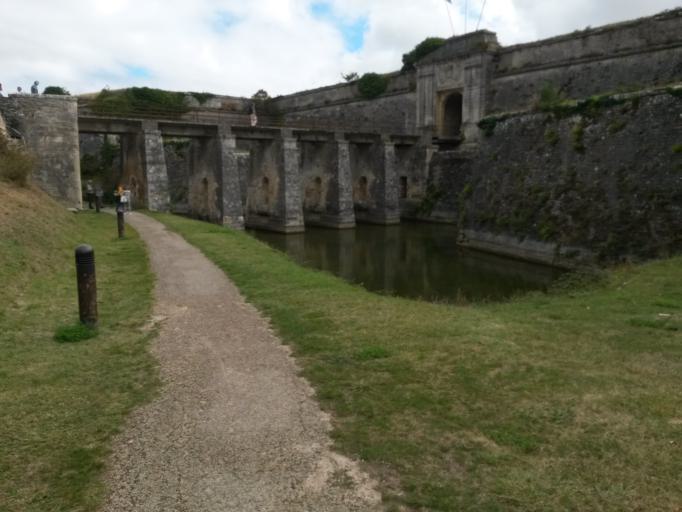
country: FR
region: Poitou-Charentes
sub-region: Departement de la Charente-Maritime
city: Saint-Trojan-les-Bains
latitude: 45.8852
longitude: -1.1905
